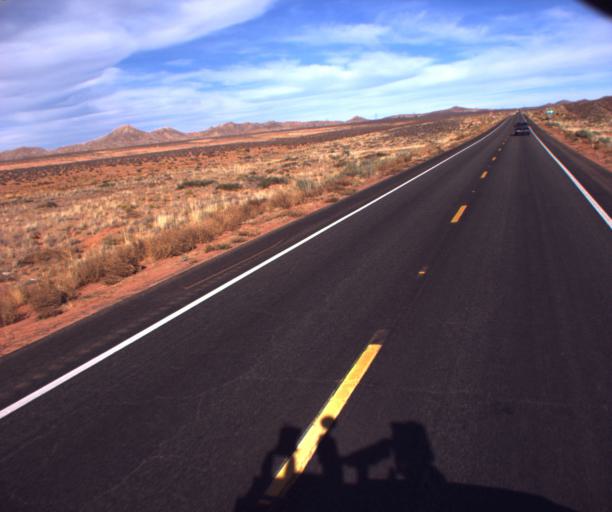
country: US
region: Arizona
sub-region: Apache County
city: Many Farms
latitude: 36.9270
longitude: -109.5843
